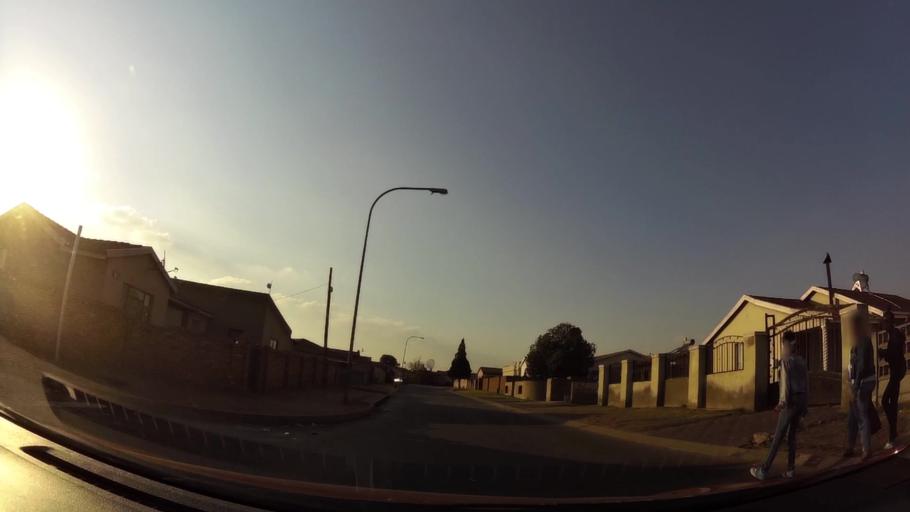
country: ZA
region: Gauteng
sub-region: City of Johannesburg Metropolitan Municipality
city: Soweto
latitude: -26.2868
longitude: 27.8953
